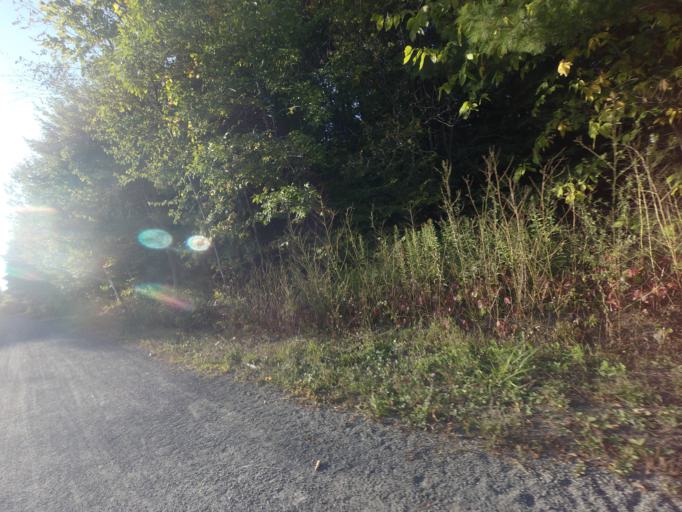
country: CA
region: Quebec
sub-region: Laurentides
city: Saint-Jerome
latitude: 45.8095
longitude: -74.0318
